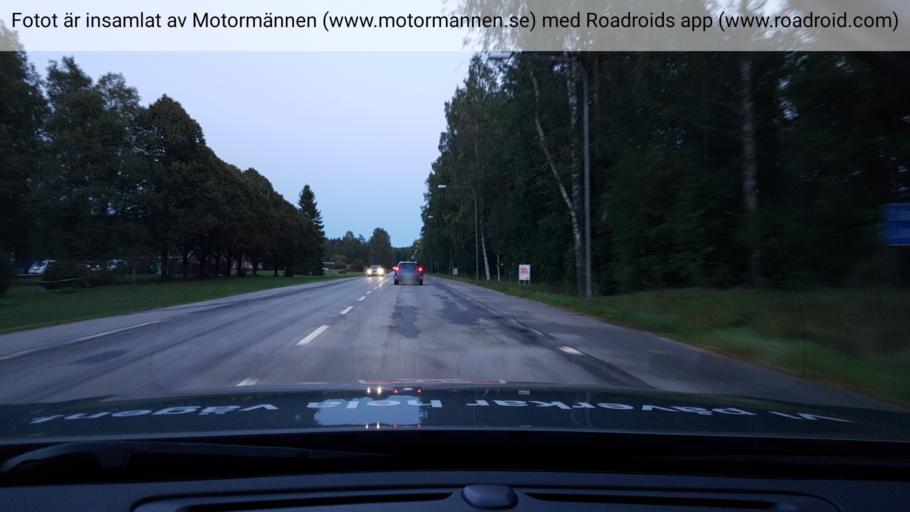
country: SE
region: OErebro
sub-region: Ljusnarsbergs Kommun
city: Kopparberg
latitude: 59.8715
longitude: 15.0082
